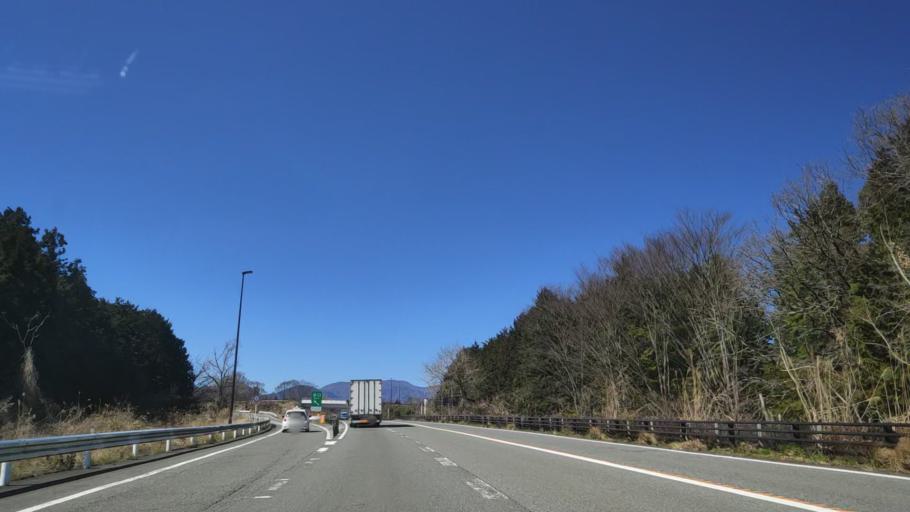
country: JP
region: Shizuoka
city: Fujinomiya
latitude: 35.2706
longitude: 138.6141
